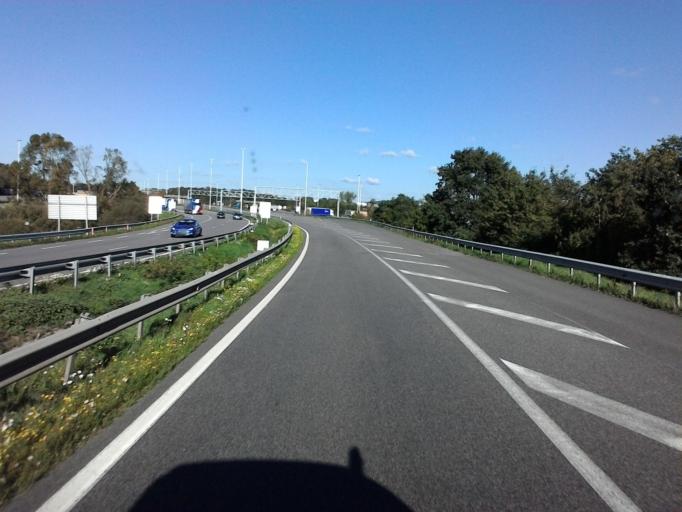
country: FR
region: Lorraine
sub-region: Departement de Meurthe-et-Moselle
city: Mont-Saint-Martin
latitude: 49.5481
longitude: 5.8041
